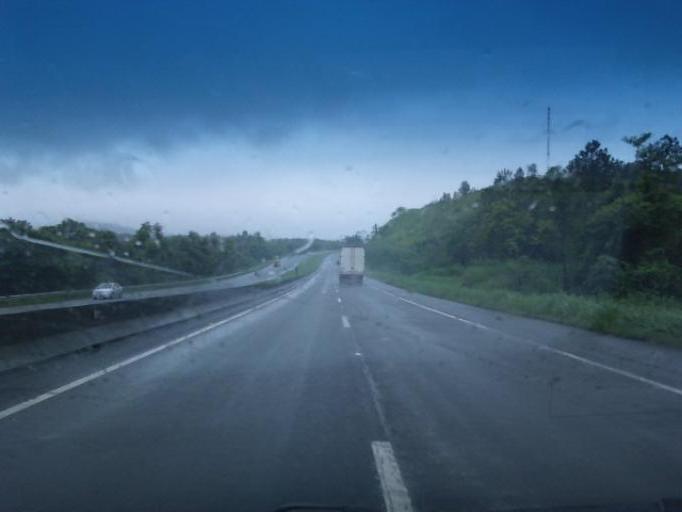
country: BR
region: Sao Paulo
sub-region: Cajati
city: Cajati
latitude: -24.7580
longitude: -48.1636
